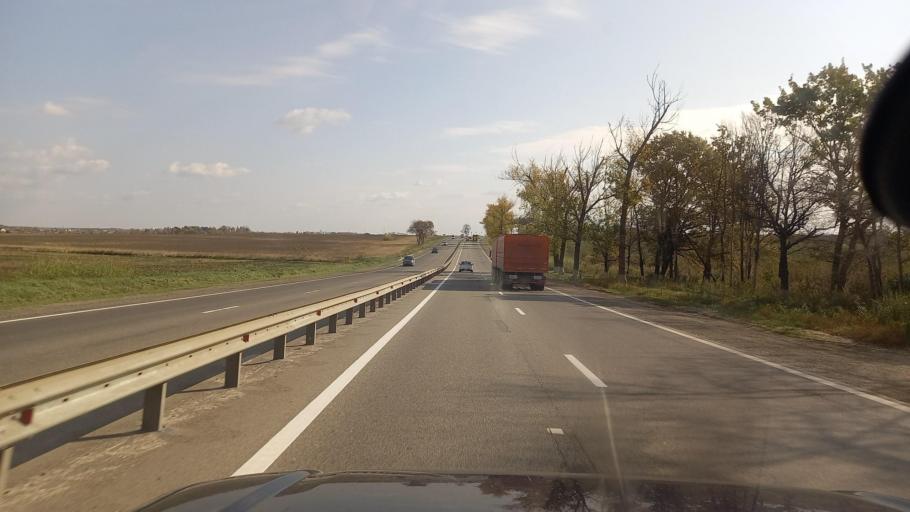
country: RU
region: Krasnodarskiy
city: Akhtyrskiy
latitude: 44.8543
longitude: 38.2573
